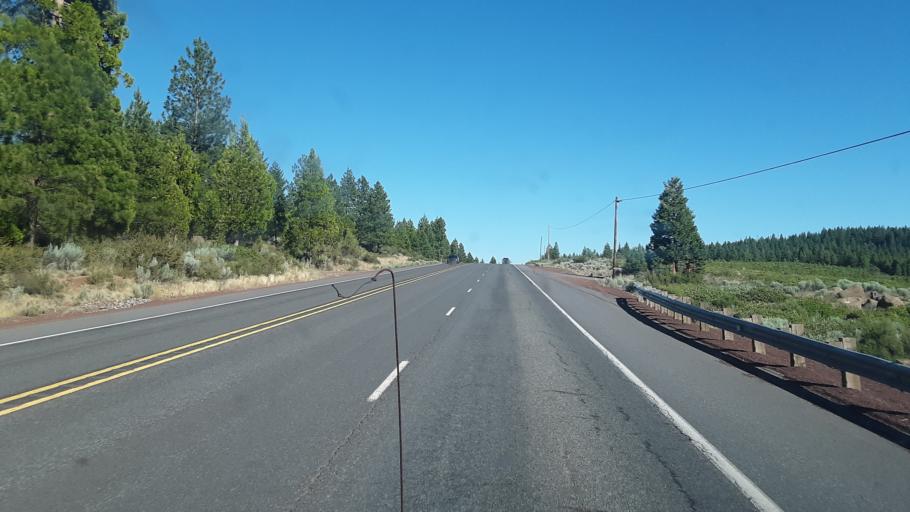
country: US
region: Oregon
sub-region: Klamath County
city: Klamath Falls
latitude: 42.3553
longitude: -121.9864
